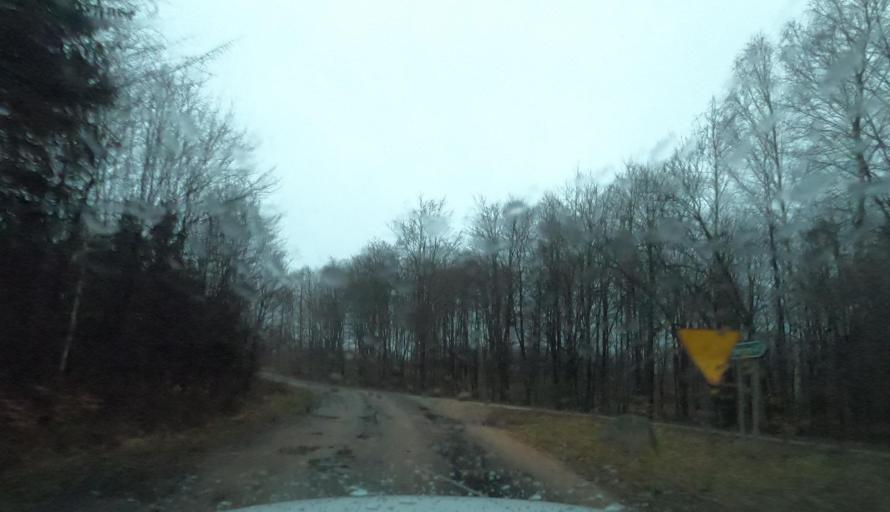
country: PL
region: West Pomeranian Voivodeship
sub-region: Powiat szczecinecki
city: Borne Sulinowo
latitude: 53.6905
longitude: 16.4806
